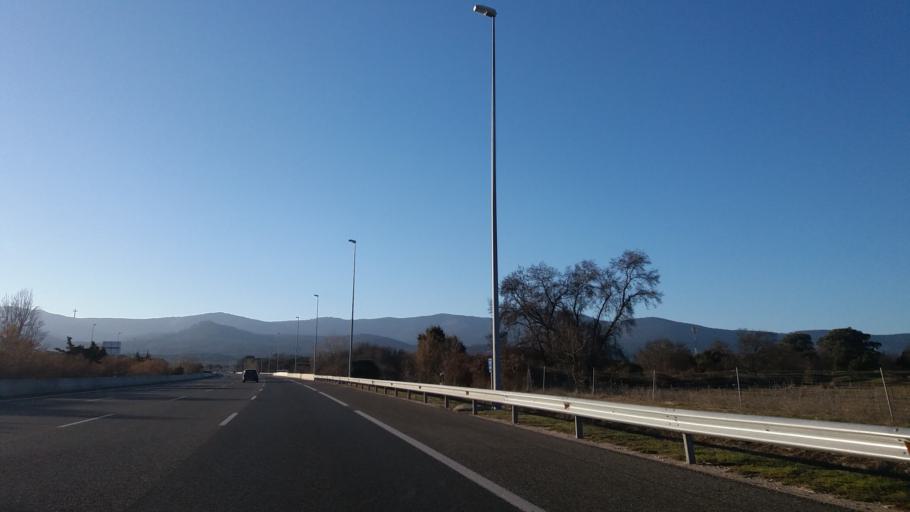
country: ES
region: Madrid
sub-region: Provincia de Madrid
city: Alpedrete
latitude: 40.6486
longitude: -4.0593
